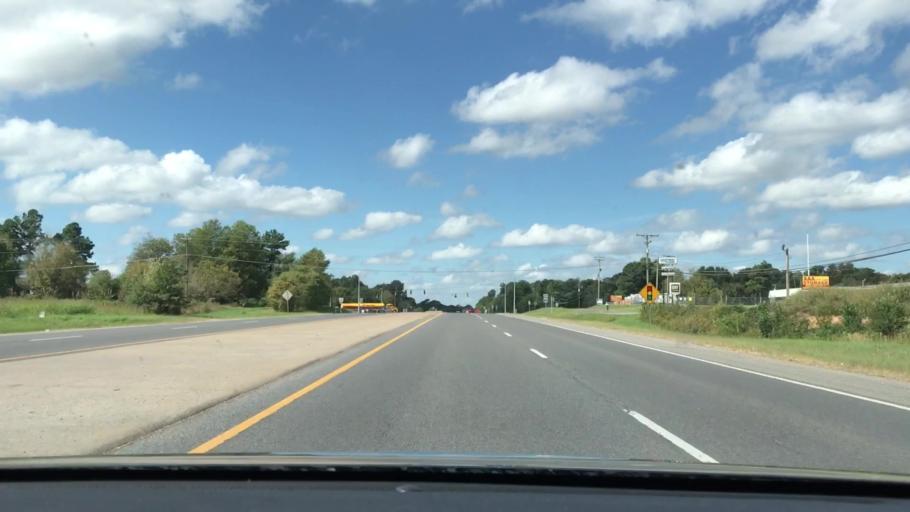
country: US
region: Kentucky
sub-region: McCracken County
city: Reidland
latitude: 37.0090
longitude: -88.5054
